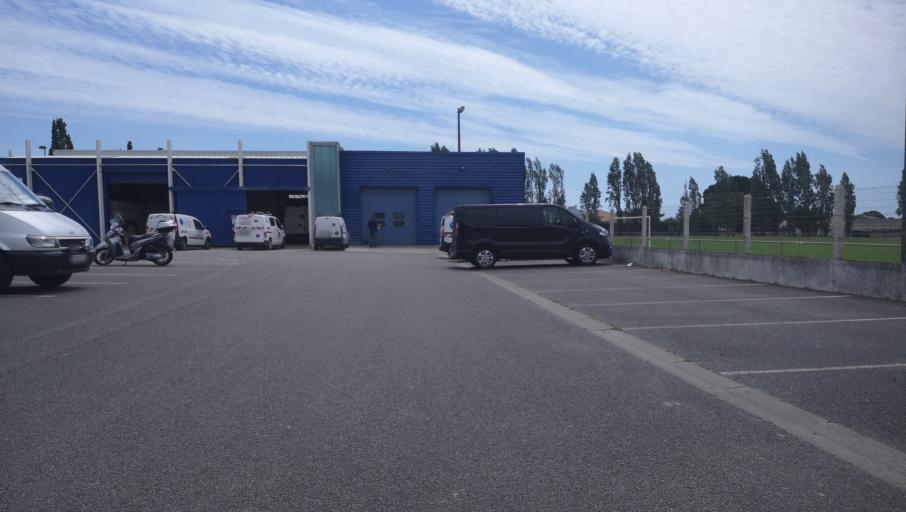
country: FR
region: Pays de la Loire
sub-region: Departement de la Vendee
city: Les Sables-d'Olonne
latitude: 46.5103
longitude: -1.7731
